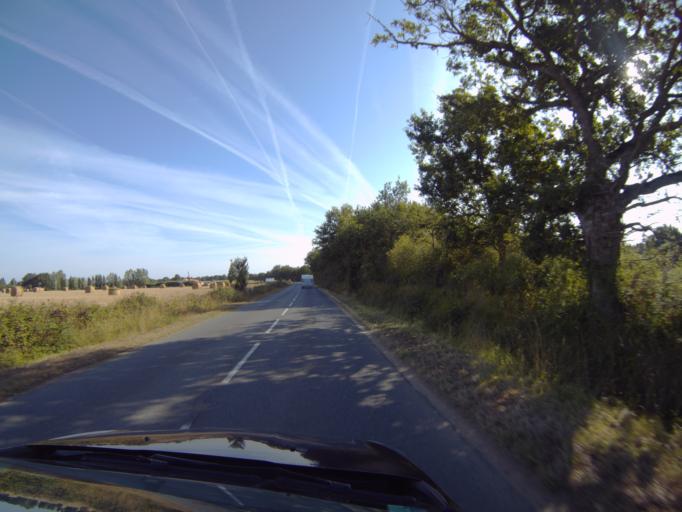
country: FR
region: Pays de la Loire
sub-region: Departement de la Vendee
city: Saint-Hilaire-de-Talmont
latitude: 46.4845
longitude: -1.5867
